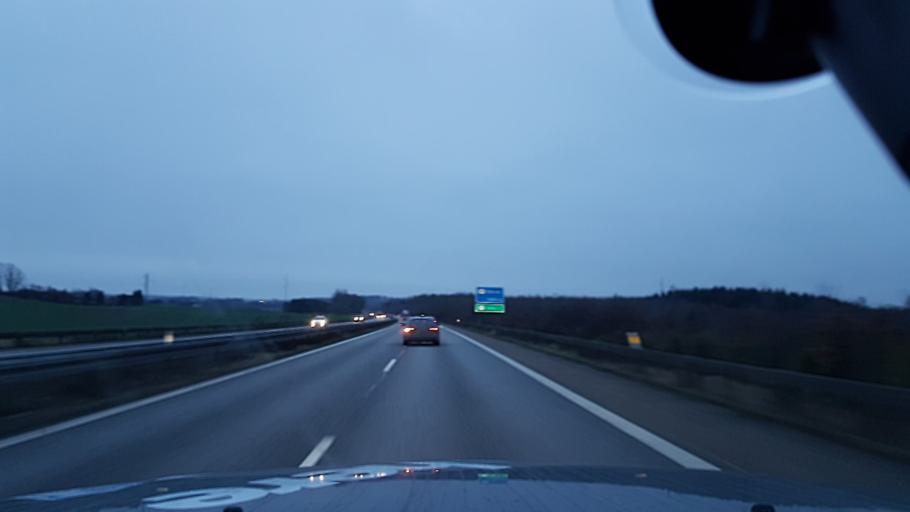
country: DK
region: Zealand
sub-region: Vordingborg Kommune
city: Orslev
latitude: 55.1421
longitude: 11.9380
